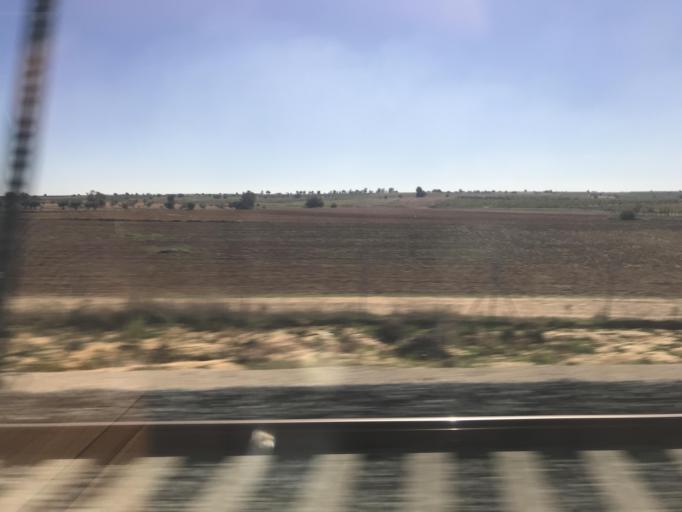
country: ES
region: Castille-La Mancha
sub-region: Provincia de Cuenca
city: Zarza de Tajo
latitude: 39.9818
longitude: -3.1267
